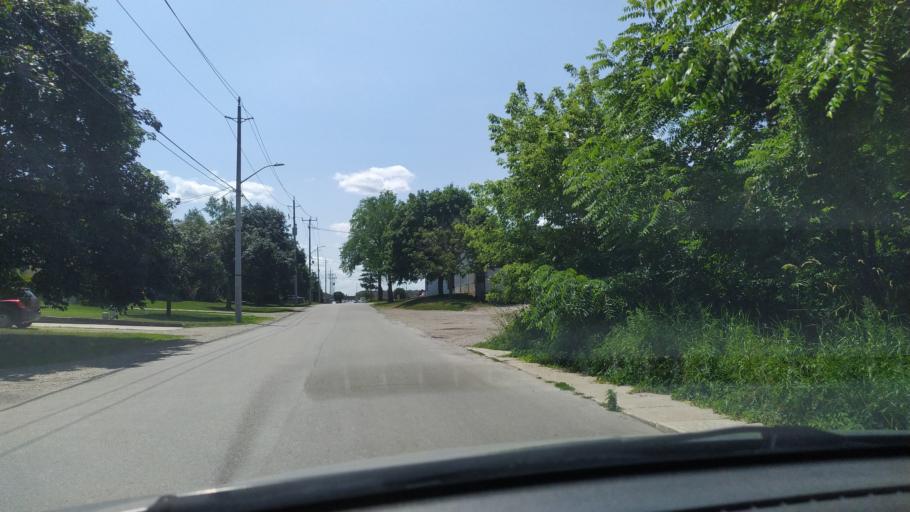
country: CA
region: Ontario
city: Stratford
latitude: 43.3574
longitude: -80.9917
